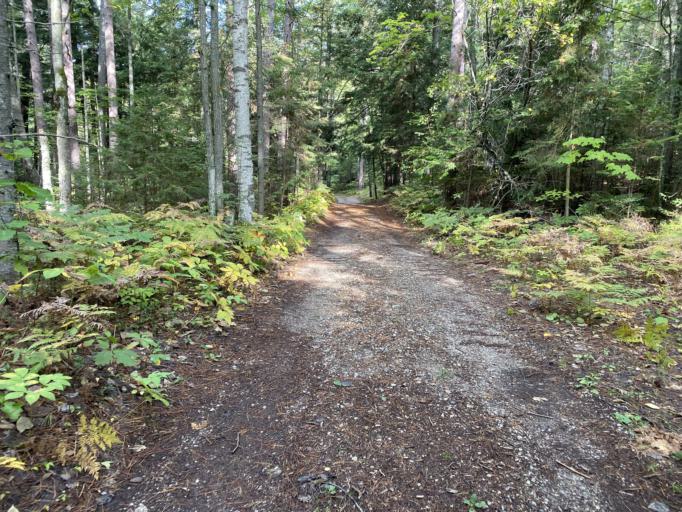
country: US
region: Michigan
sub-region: Mackinac County
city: Saint Ignace
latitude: 45.7469
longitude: -84.8785
